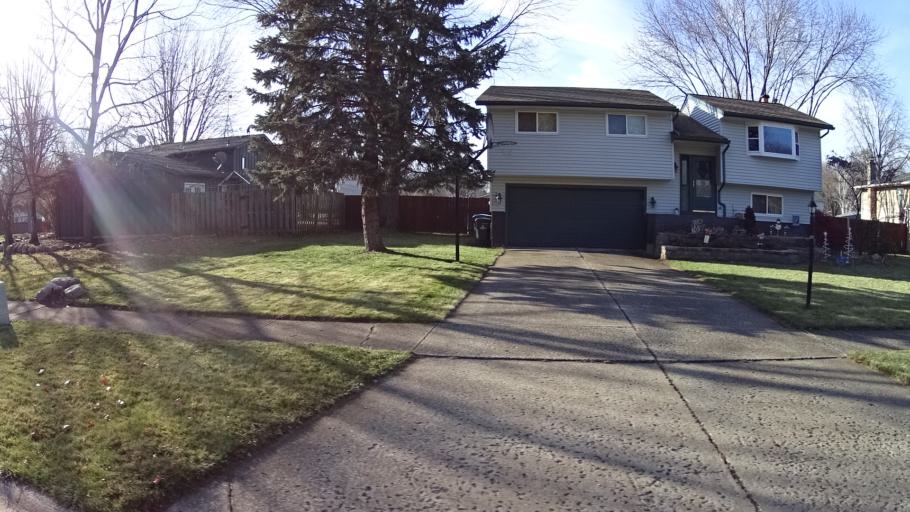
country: US
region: Ohio
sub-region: Lorain County
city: North Ridgeville
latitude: 41.3896
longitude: -81.9897
